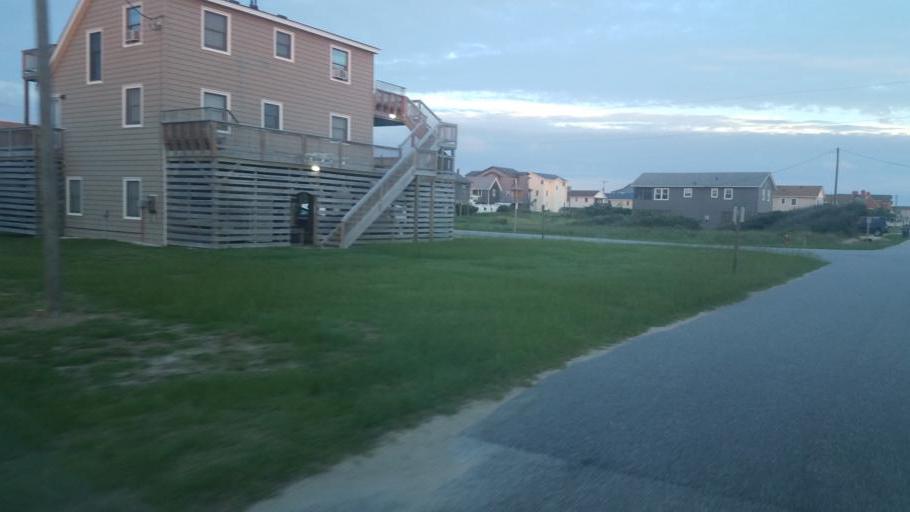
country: US
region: North Carolina
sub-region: Dare County
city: Kitty Hawk
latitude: 36.0757
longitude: -75.6978
